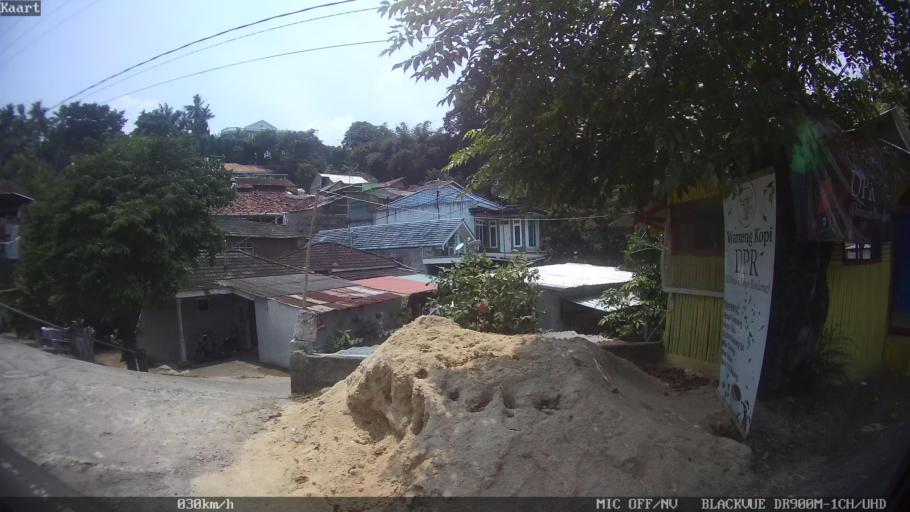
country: ID
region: Lampung
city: Bandarlampung
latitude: -5.4329
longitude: 105.2729
